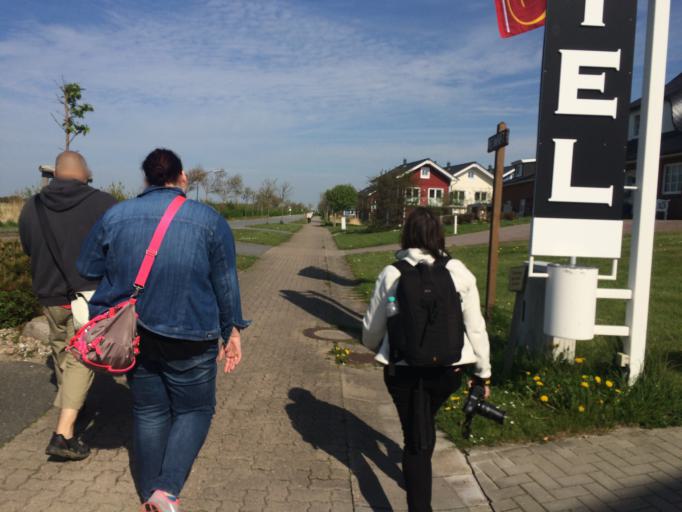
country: DE
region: Schleswig-Holstein
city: Dagebull
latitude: 54.7298
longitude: 8.6997
